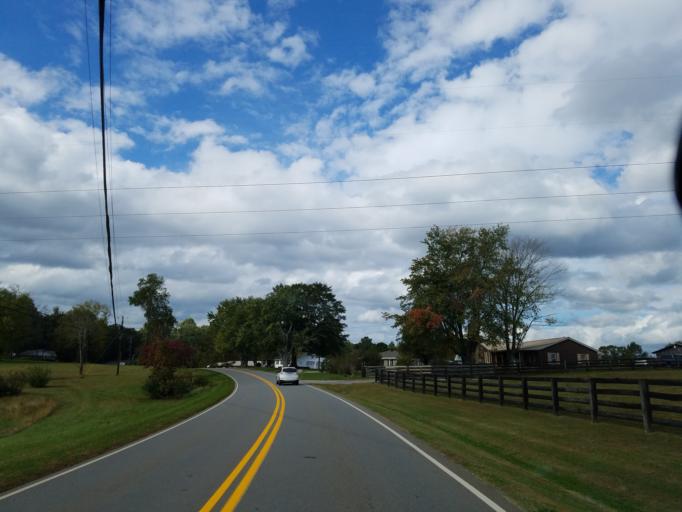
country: US
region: Georgia
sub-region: Pickens County
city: Jasper
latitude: 34.4252
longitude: -84.4192
